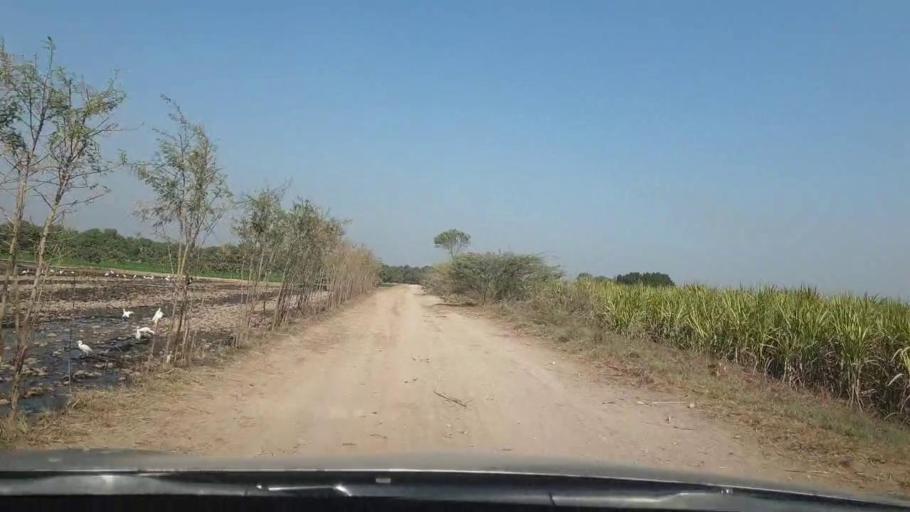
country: PK
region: Sindh
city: Tando Allahyar
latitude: 25.5957
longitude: 68.6408
